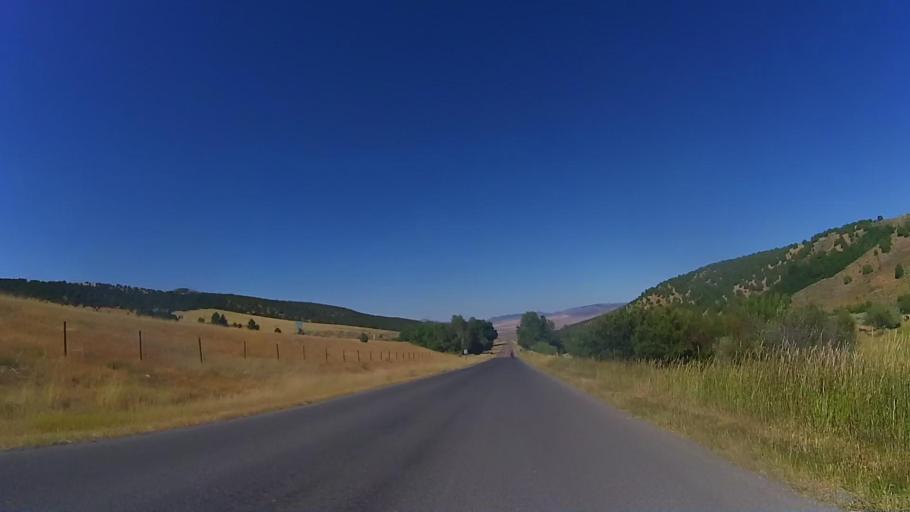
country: US
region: Idaho
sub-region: Oneida County
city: Malad City
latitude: 42.3497
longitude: -112.2247
